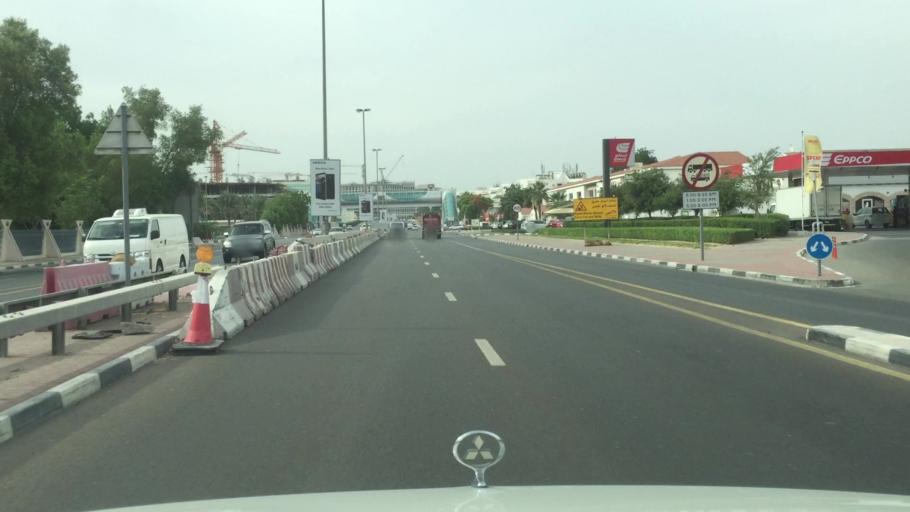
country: AE
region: Ash Shariqah
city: Sharjah
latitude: 25.2414
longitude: 55.3446
